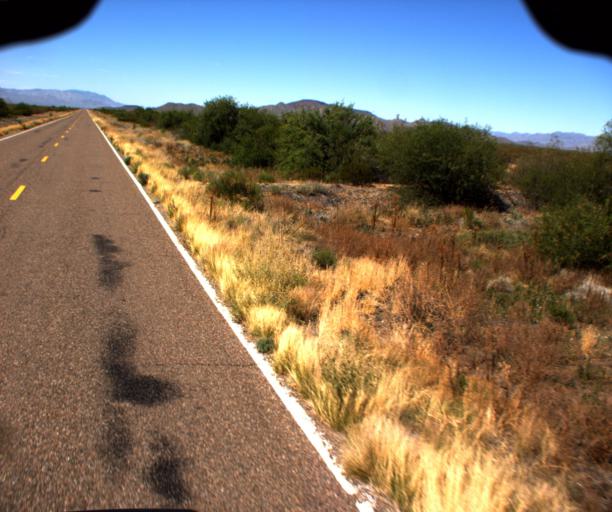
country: US
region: Arizona
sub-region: Yavapai County
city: Congress
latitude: 34.0666
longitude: -113.0381
